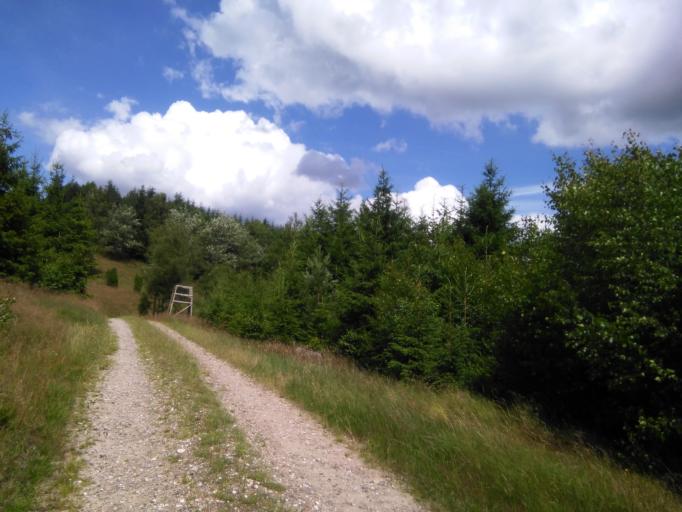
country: DK
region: Central Jutland
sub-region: Silkeborg Kommune
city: Virklund
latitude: 56.0676
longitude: 9.4486
